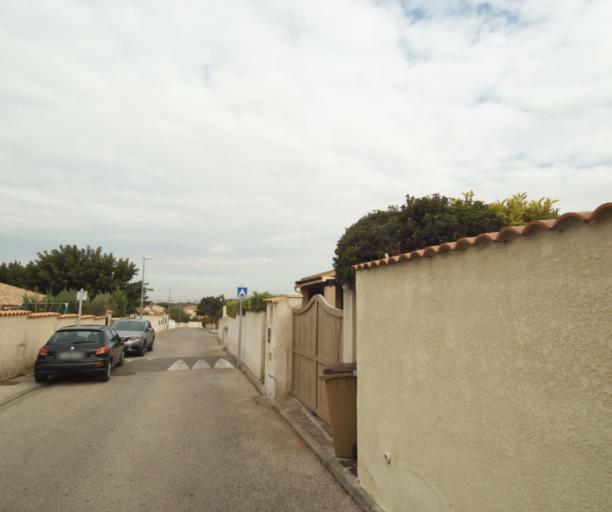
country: FR
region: Provence-Alpes-Cote d'Azur
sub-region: Departement des Bouches-du-Rhone
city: Saint-Victoret
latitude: 43.4111
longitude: 5.2650
